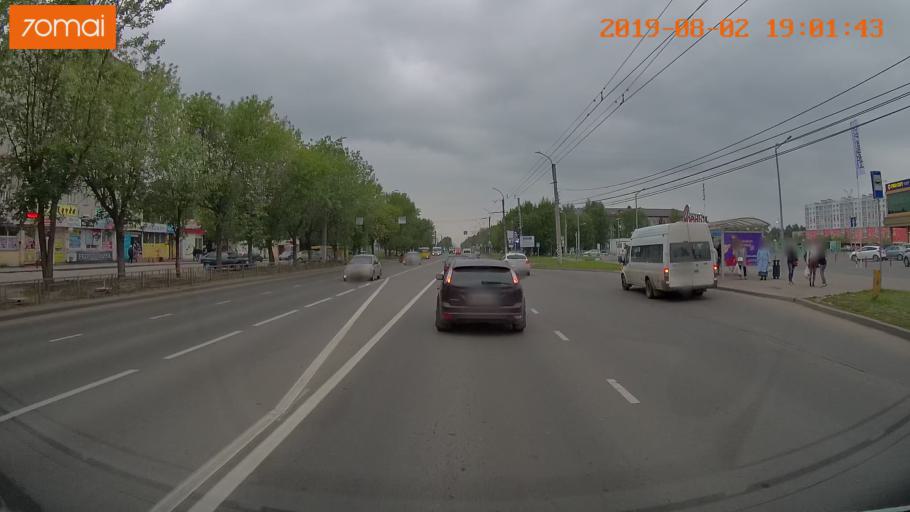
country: RU
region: Ivanovo
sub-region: Gorod Ivanovo
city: Ivanovo
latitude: 56.9637
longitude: 40.9896
